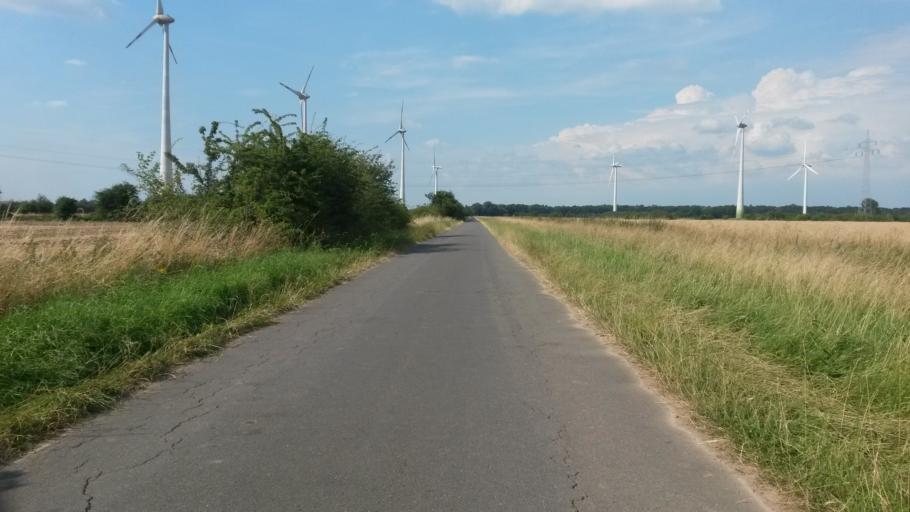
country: DE
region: Lower Saxony
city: Riede
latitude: 53.0170
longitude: 8.9293
